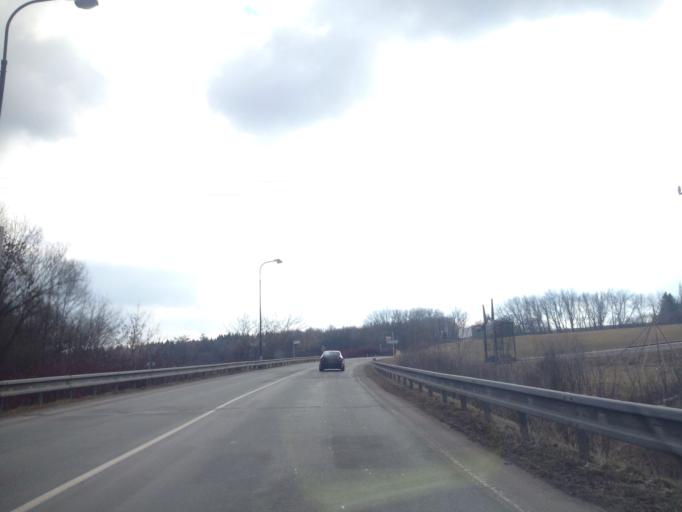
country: CZ
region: Kralovehradecky
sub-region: Okres Trutnov
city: Vrchlabi
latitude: 50.6112
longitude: 15.6036
